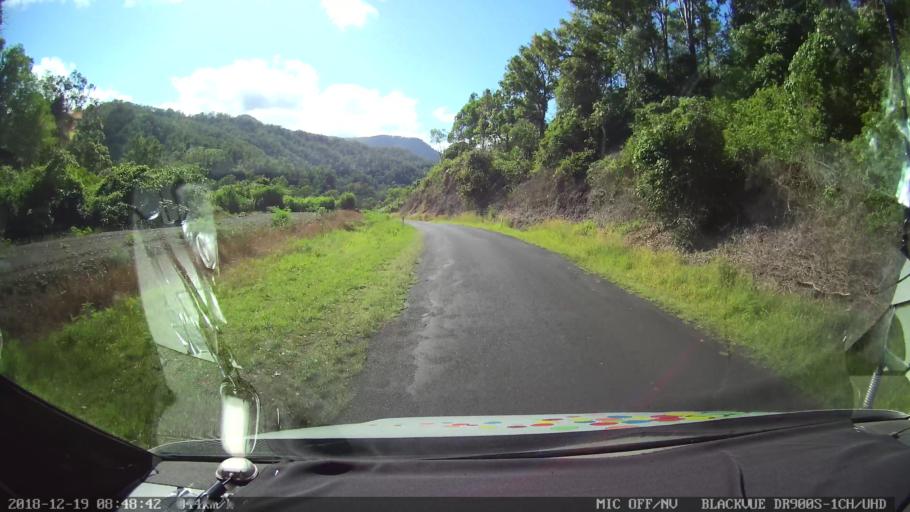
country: AU
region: New South Wales
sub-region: Kyogle
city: Kyogle
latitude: -28.3724
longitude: 152.9719
